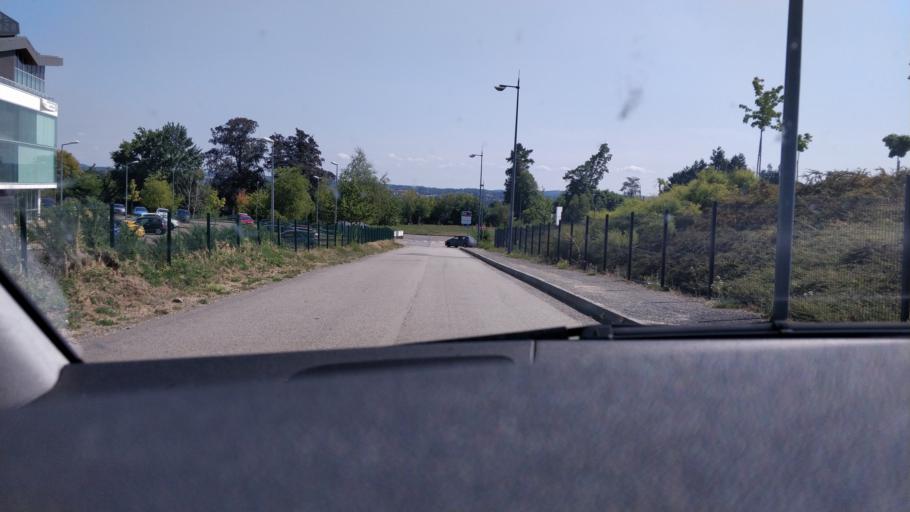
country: FR
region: Limousin
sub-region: Departement de la Haute-Vienne
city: Le Palais-sur-Vienne
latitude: 45.8564
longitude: 1.2872
